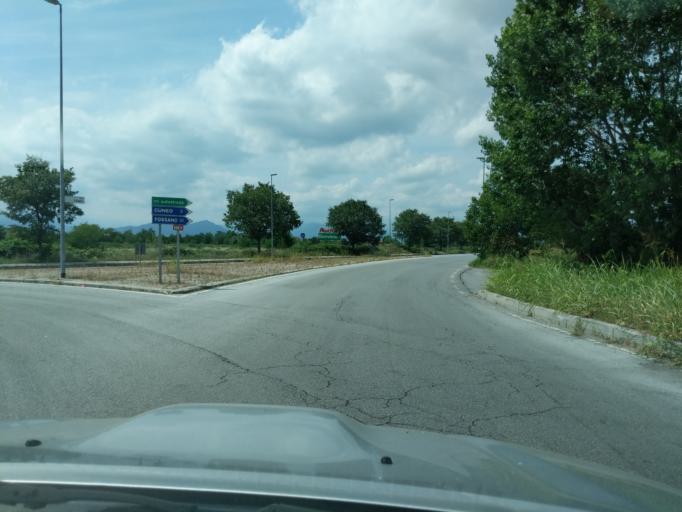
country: IT
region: Piedmont
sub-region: Provincia di Cuneo
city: Cuneo
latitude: 44.3960
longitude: 7.5881
